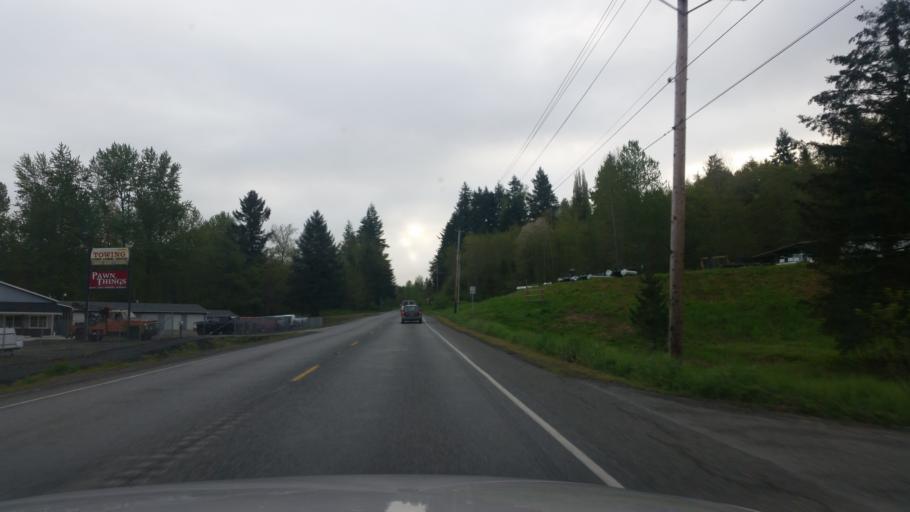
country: US
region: Washington
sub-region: Pierce County
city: Eatonville
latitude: 46.8765
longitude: -122.2804
